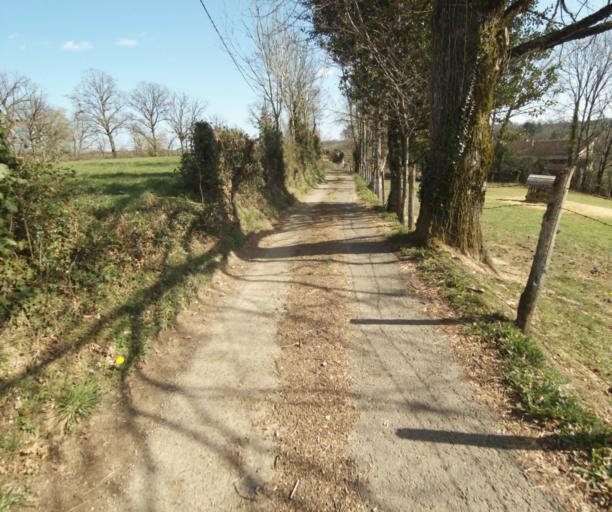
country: FR
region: Limousin
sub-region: Departement de la Correze
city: Saint-Mexant
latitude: 45.3089
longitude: 1.6415
